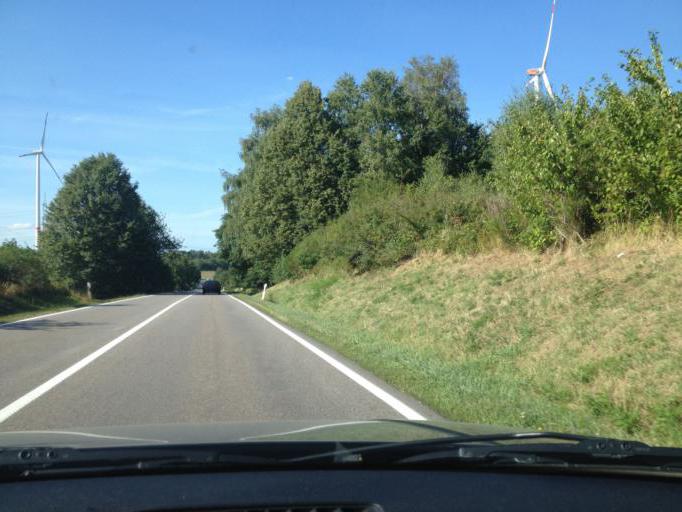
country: DE
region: Saarland
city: Schiffweiler
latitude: 49.3766
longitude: 7.1471
